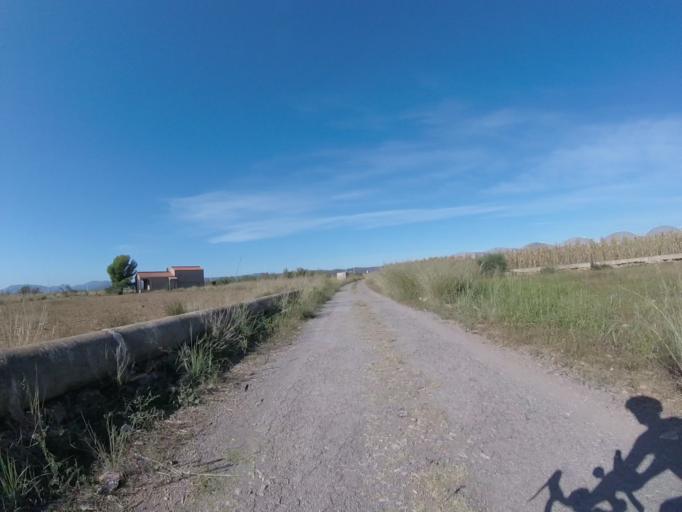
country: ES
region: Valencia
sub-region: Provincia de Castello
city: Torreblanca
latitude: 40.2102
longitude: 0.2267
